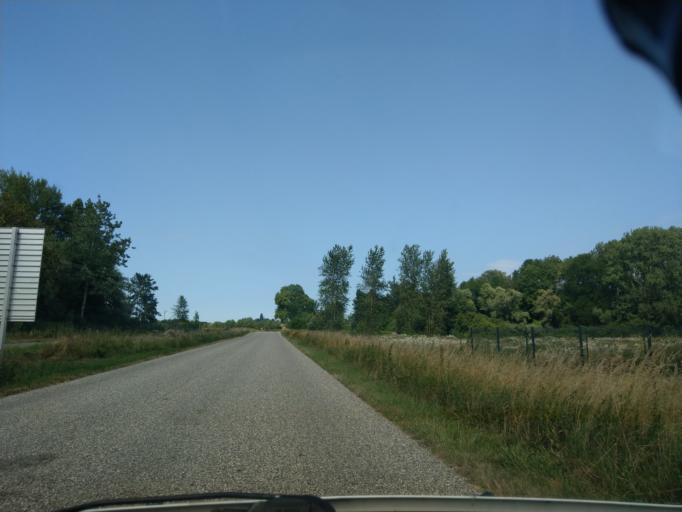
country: FR
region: Alsace
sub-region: Departement du Bas-Rhin
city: Roppenheim
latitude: 48.8199
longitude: 8.0220
